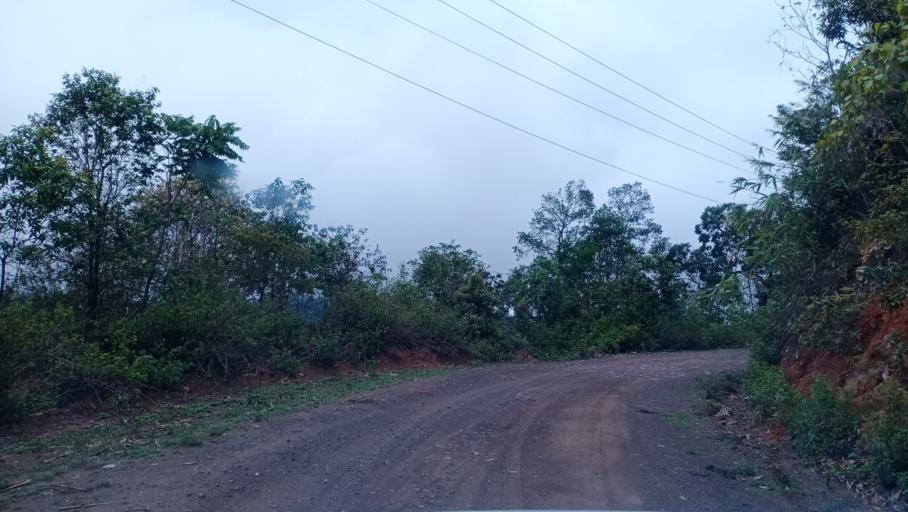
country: LA
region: Phongsali
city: Phongsali
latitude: 21.3488
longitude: 102.0966
